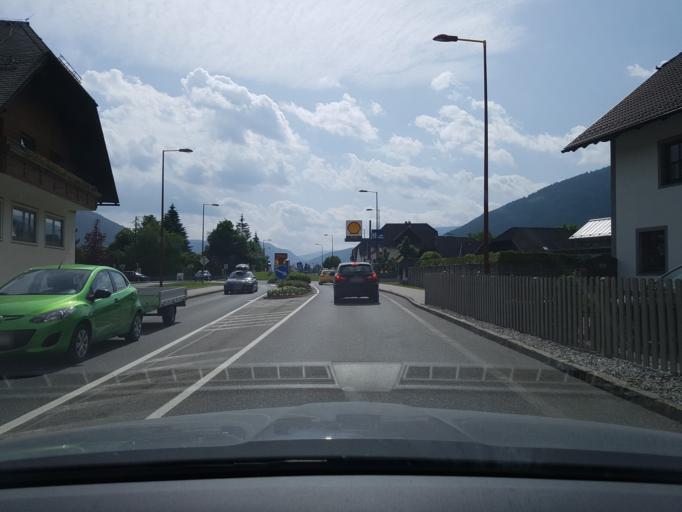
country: AT
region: Salzburg
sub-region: Politischer Bezirk Tamsweg
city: Sankt Michael im Lungau
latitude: 47.0958
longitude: 13.6360
